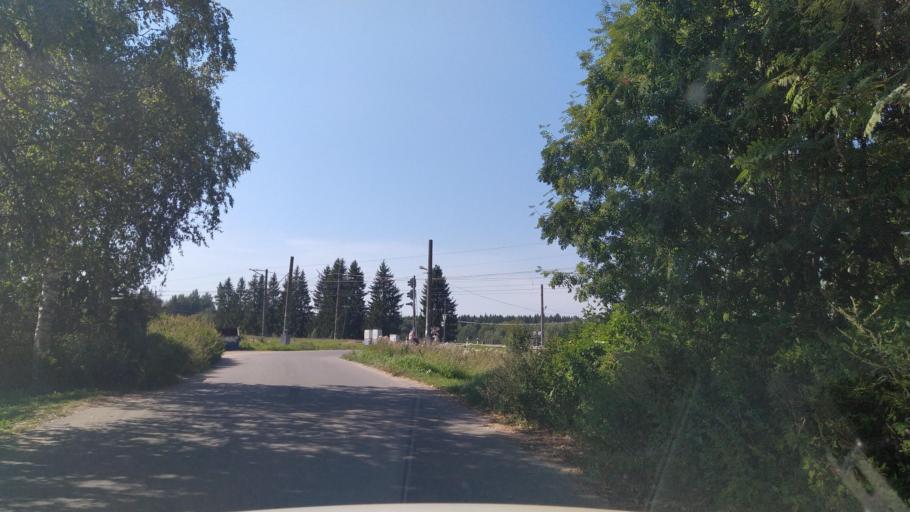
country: RU
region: Leningrad
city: Rozhdestveno
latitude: 59.2622
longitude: 30.0314
